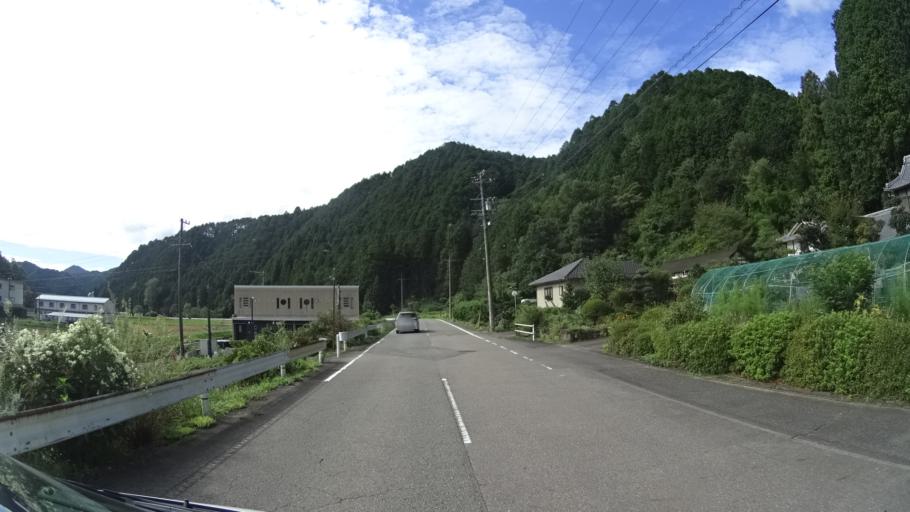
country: JP
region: Gifu
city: Minokamo
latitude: 35.5848
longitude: 137.0842
